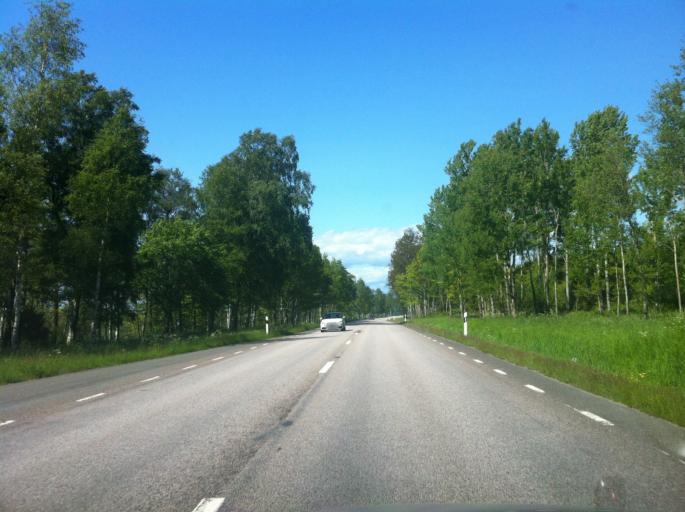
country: SE
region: Vaestra Goetaland
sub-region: Gullspangs Kommun
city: Gullspang
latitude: 59.0270
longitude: 14.1254
